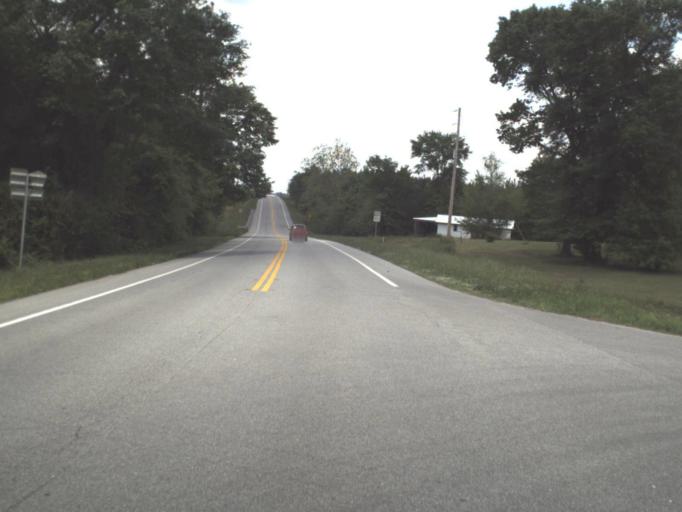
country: US
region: Alabama
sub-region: Escambia County
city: Atmore
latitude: 30.9232
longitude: -87.4806
